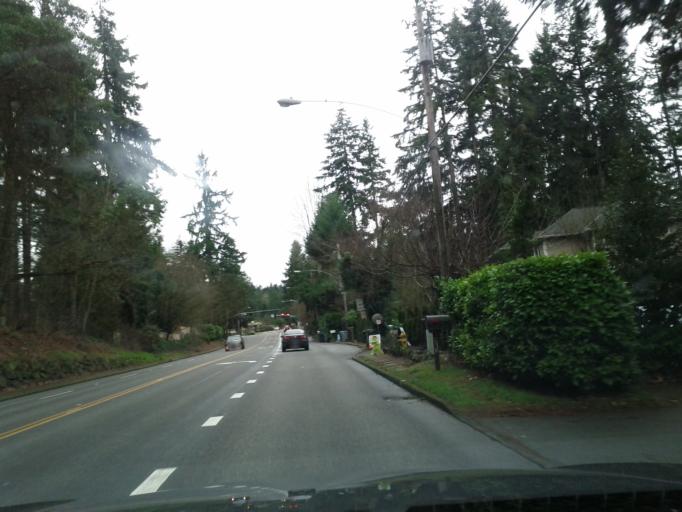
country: US
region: Washington
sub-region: King County
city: Eastgate
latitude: 47.5728
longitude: -122.1411
